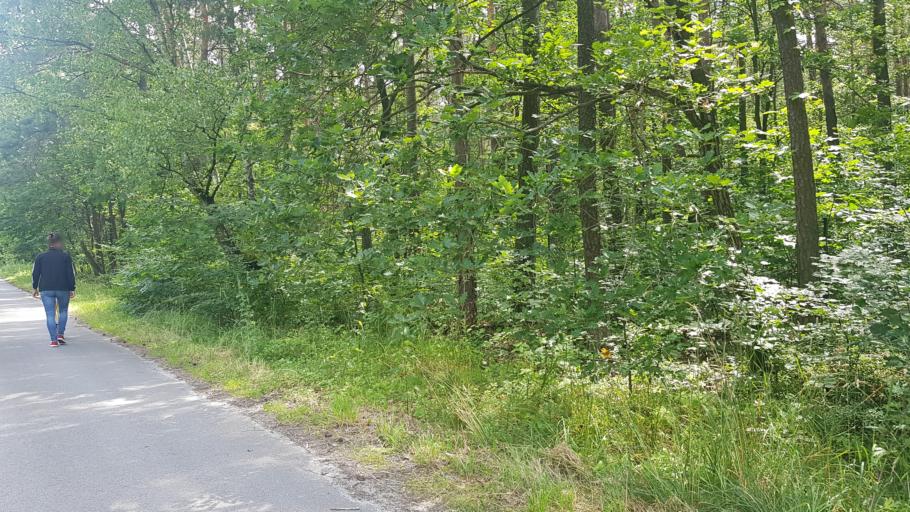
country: PL
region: Opole Voivodeship
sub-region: Powiat opolski
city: Chrzastowice
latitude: 50.7011
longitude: 18.1395
